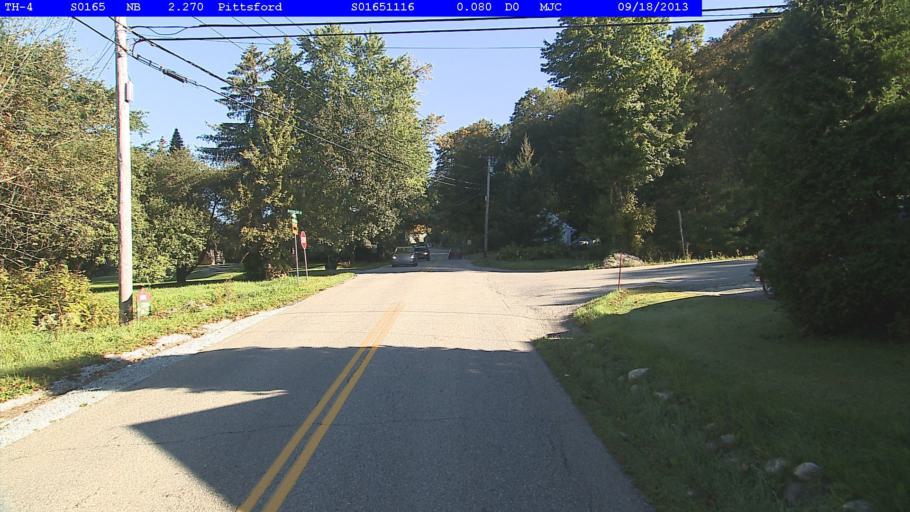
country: US
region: Vermont
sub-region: Rutland County
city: Rutland
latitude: 43.6709
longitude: -72.9428
